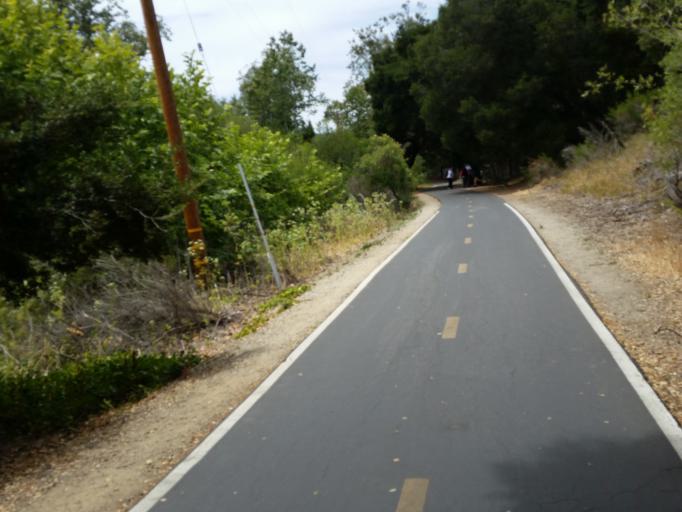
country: US
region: California
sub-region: San Luis Obispo County
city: Avila Beach
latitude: 35.1884
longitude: -120.7130
